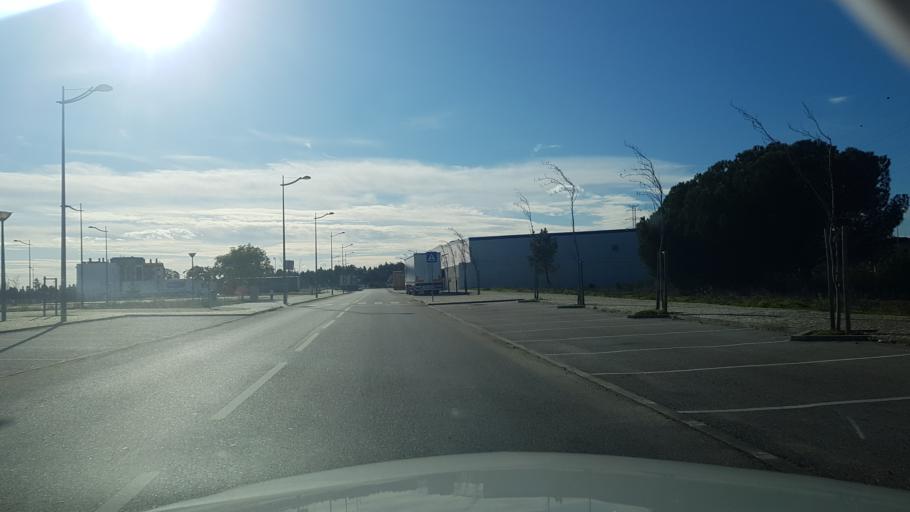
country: PT
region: Santarem
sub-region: Entroncamento
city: Entroncamento
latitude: 39.4757
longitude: -8.4839
